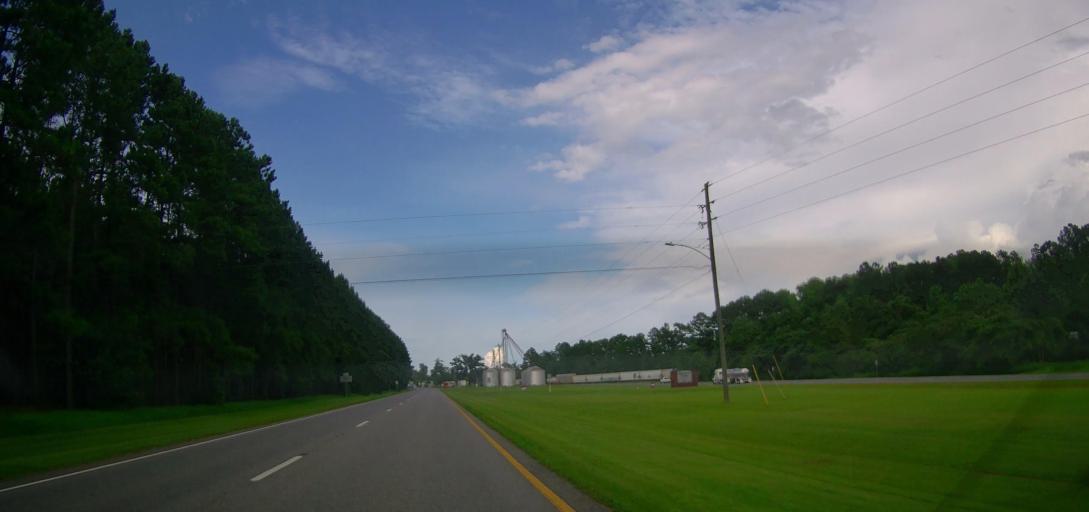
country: US
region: Georgia
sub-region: Wayne County
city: Jesup
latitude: 31.4804
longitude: -82.0246
